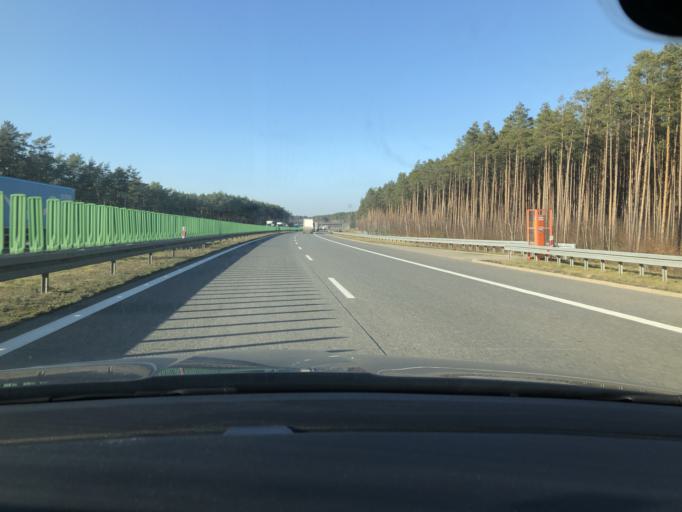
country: PL
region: Lubusz
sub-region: Powiat swiebodzinski
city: Lagow
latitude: 52.2989
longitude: 15.2608
